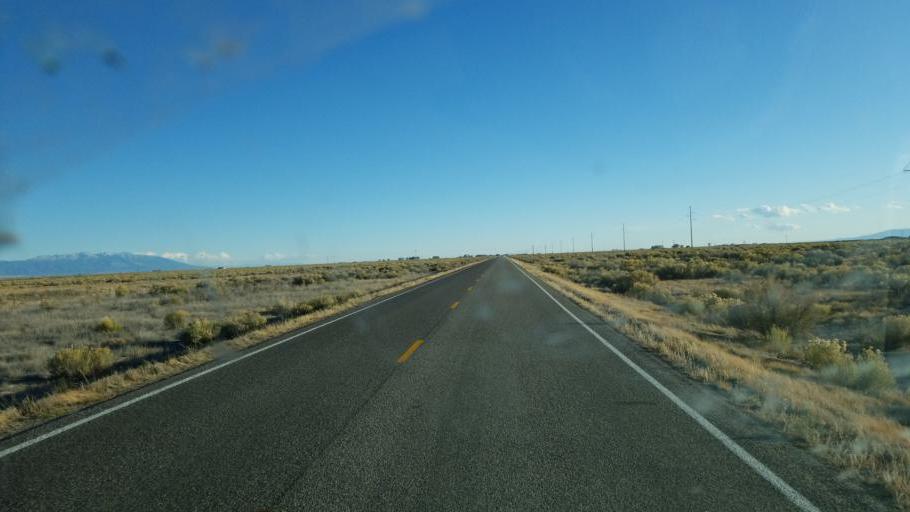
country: US
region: Colorado
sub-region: Saguache County
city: Saguache
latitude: 38.0768
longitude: -105.9171
